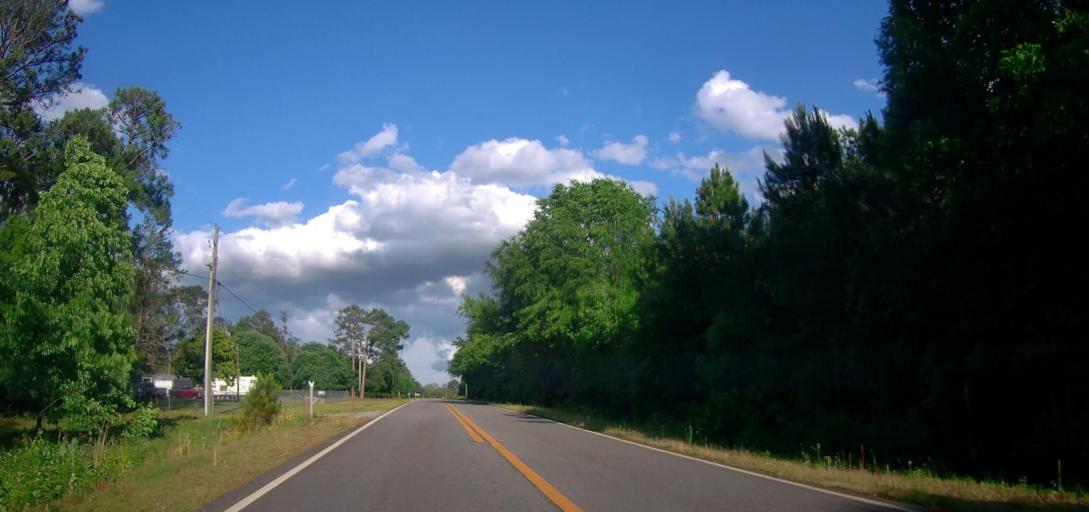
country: US
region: Georgia
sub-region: Peach County
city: Byron
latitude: 32.6762
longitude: -83.7682
